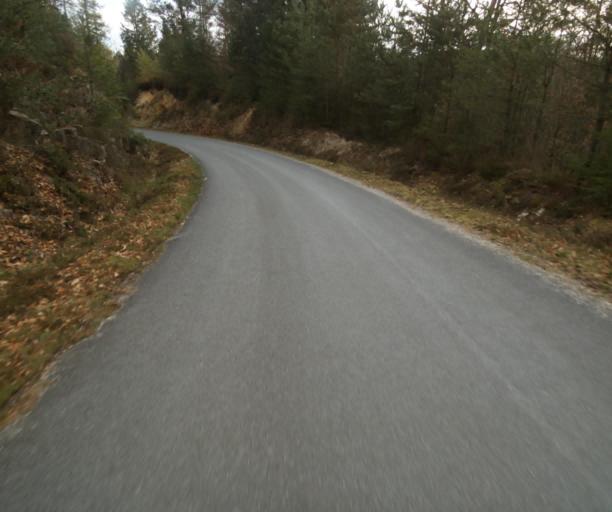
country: FR
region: Limousin
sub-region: Departement de la Correze
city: Correze
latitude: 45.4110
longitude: 1.9164
